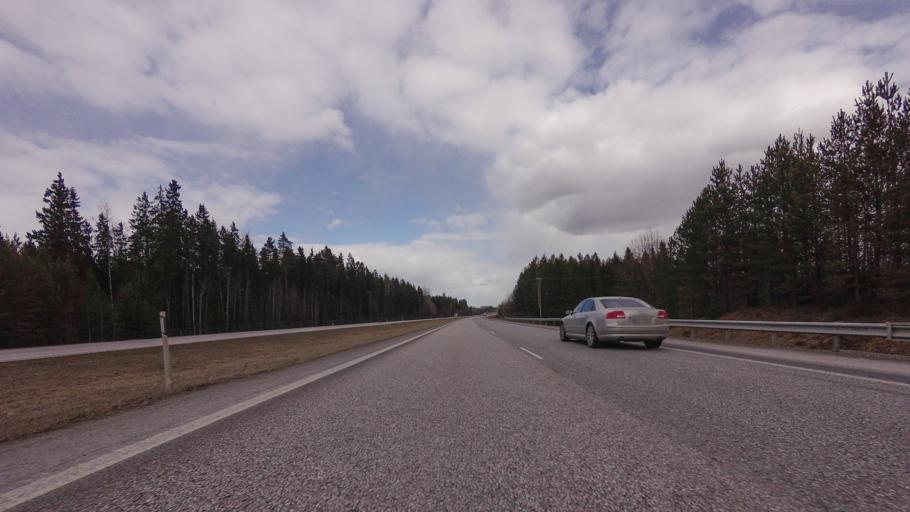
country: FI
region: Uusimaa
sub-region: Helsinki
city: Nurmijaervi
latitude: 60.4286
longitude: 24.8276
